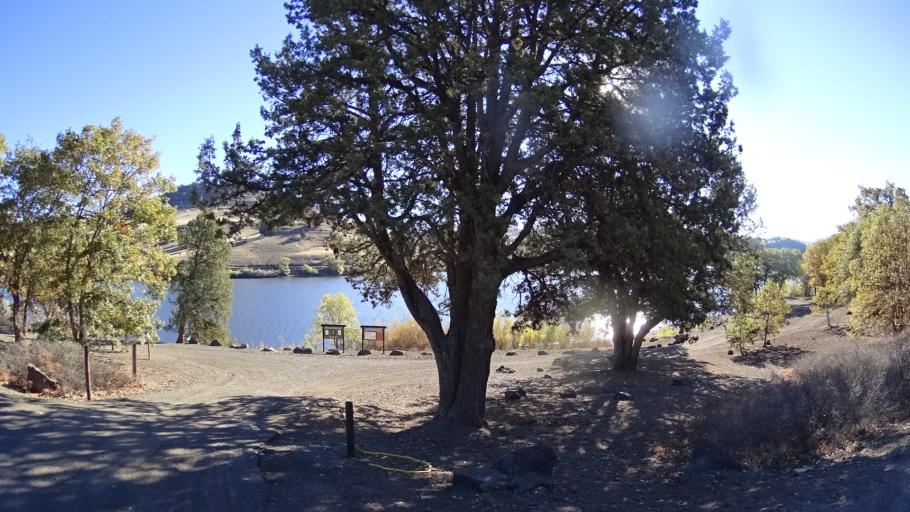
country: US
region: California
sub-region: Siskiyou County
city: Montague
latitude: 41.9681
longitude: -122.4387
